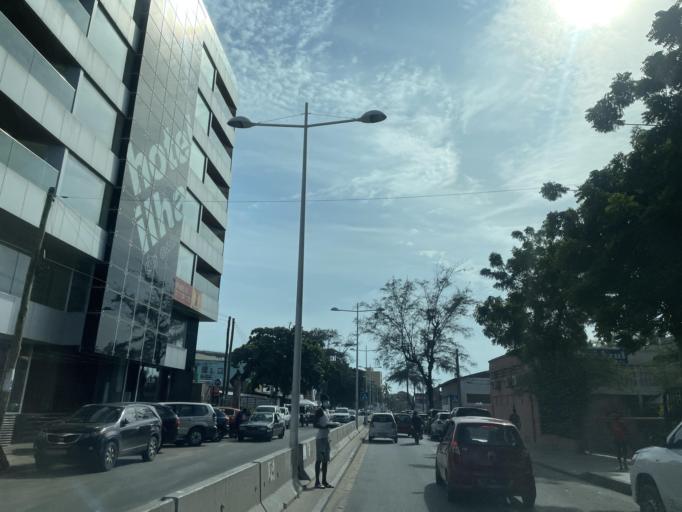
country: AO
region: Luanda
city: Luanda
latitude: -8.7777
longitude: 13.2432
